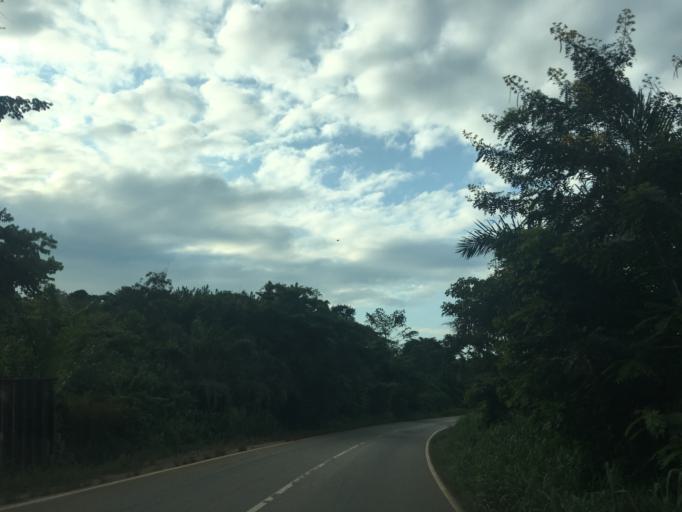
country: GH
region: Western
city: Bibiani
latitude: 6.4130
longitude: -2.3027
